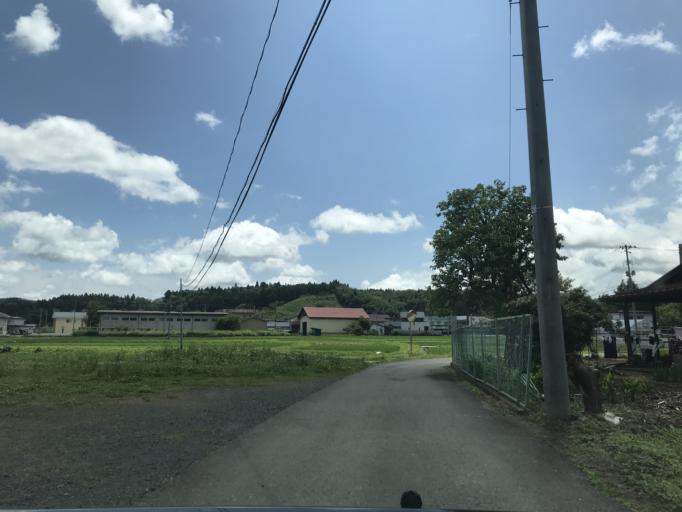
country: JP
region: Iwate
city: Ichinoseki
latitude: 38.9206
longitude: 141.0944
